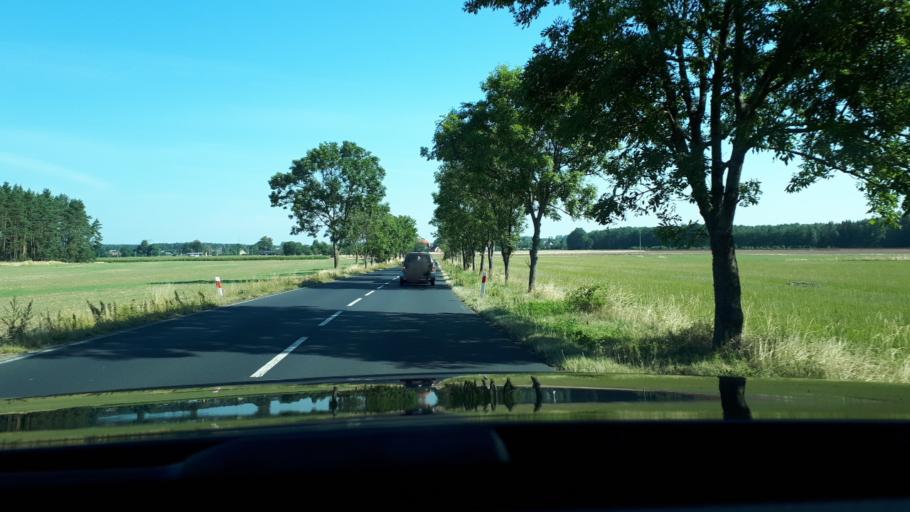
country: PL
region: Lower Silesian Voivodeship
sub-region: Powiat lubanski
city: Pisarzowice
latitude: 51.1992
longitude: 15.2461
